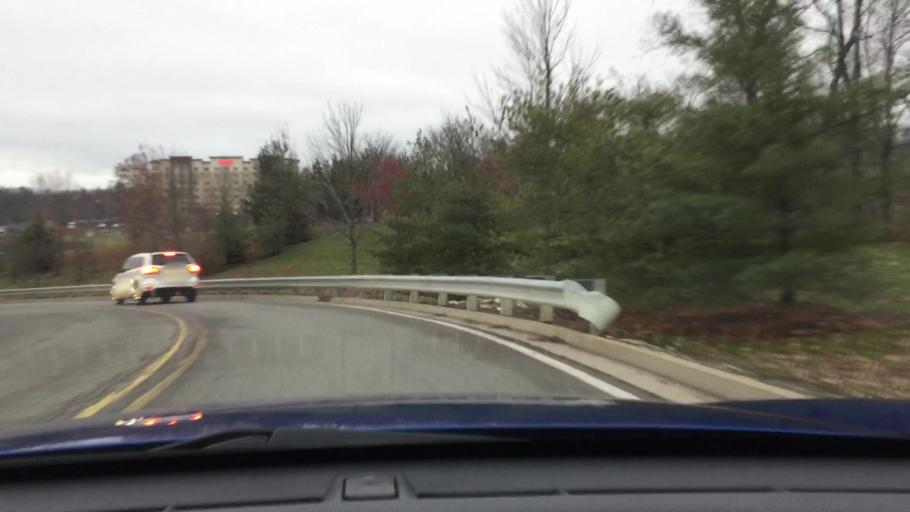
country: US
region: Pennsylvania
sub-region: Allegheny County
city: Rennerdale
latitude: 40.4414
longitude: -80.1531
